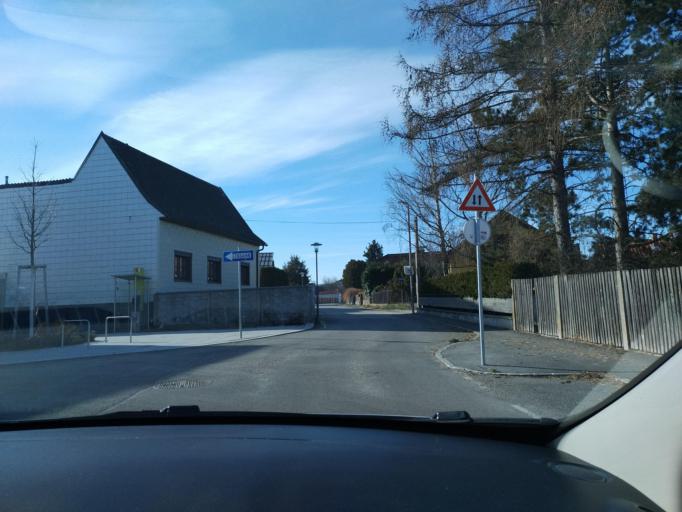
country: AT
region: Lower Austria
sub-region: Politischer Bezirk Wiener Neustadt
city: Lanzenkirchen
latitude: 47.7433
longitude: 16.2385
